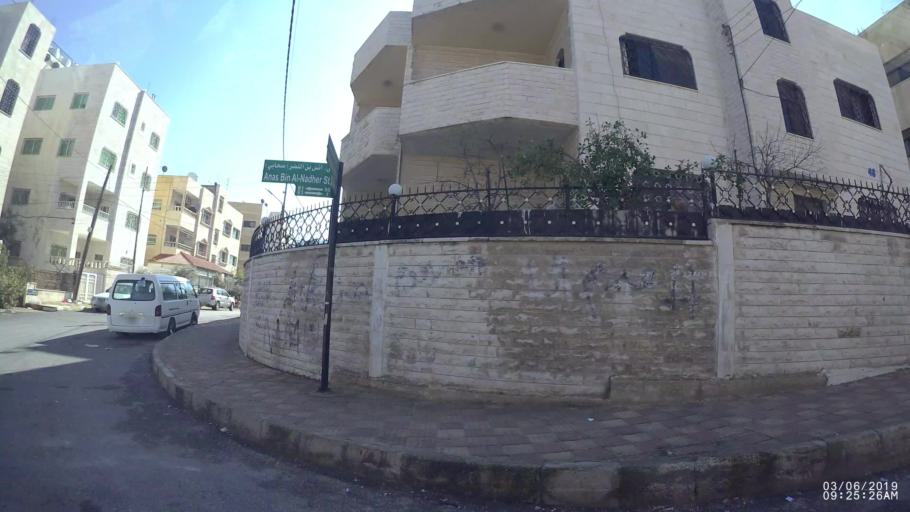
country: JO
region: Amman
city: Amman
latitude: 31.9915
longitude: 35.9888
